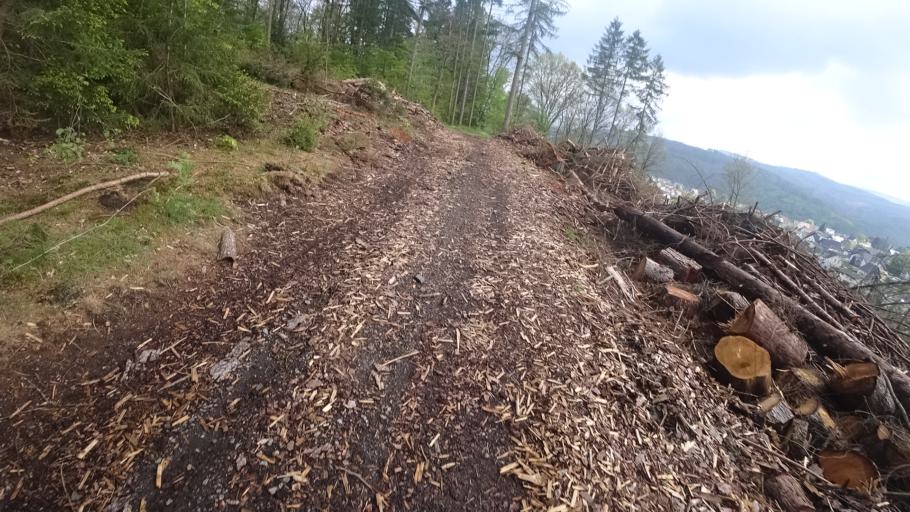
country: DE
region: Rheinland-Pfalz
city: Alsdorf
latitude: 50.7793
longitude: 7.8655
